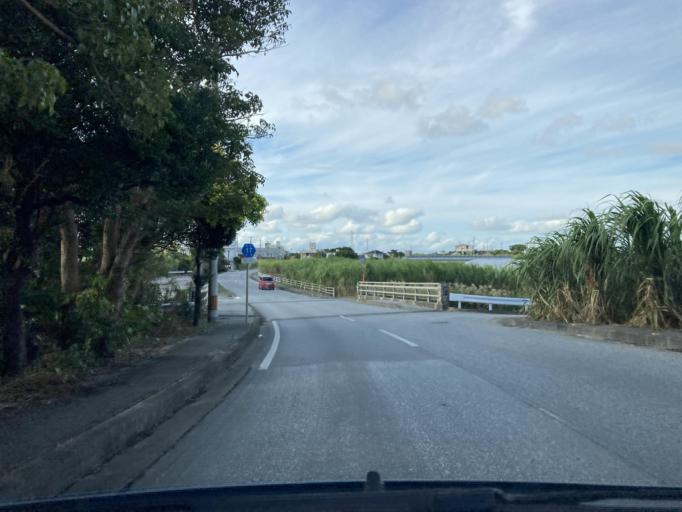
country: JP
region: Okinawa
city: Tomigusuku
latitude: 26.1506
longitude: 127.7446
